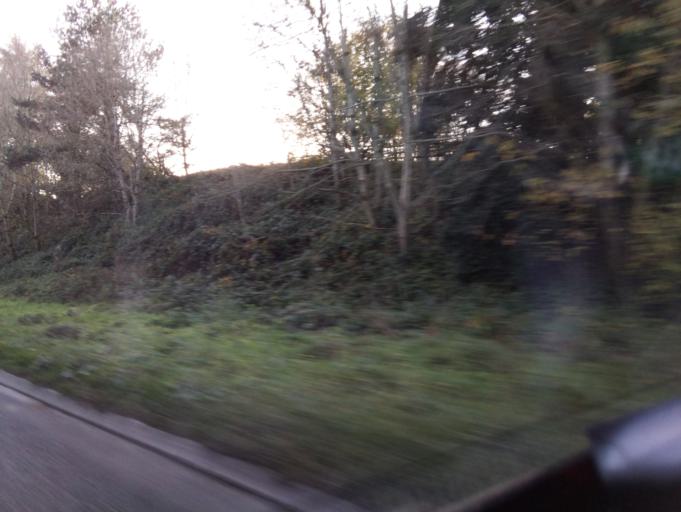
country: GB
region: England
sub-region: Wiltshire
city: Warminster
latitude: 51.1831
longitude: -2.1932
